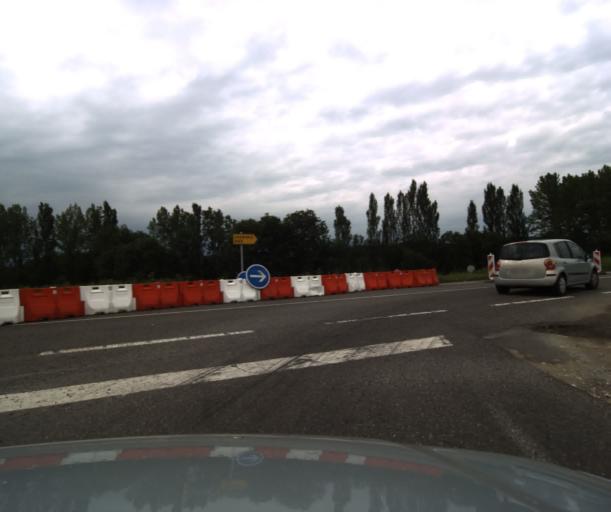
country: FR
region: Midi-Pyrenees
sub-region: Departement des Hautes-Pyrenees
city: Ossun
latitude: 43.1612
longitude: -0.0147
